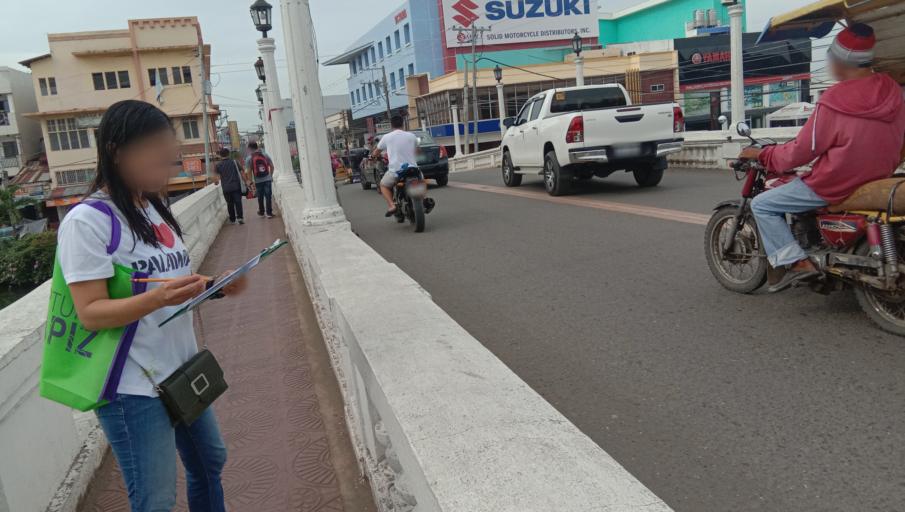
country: PH
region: Western Visayas
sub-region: Province of Capiz
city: Roxas City
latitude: 11.5825
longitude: 122.7532
